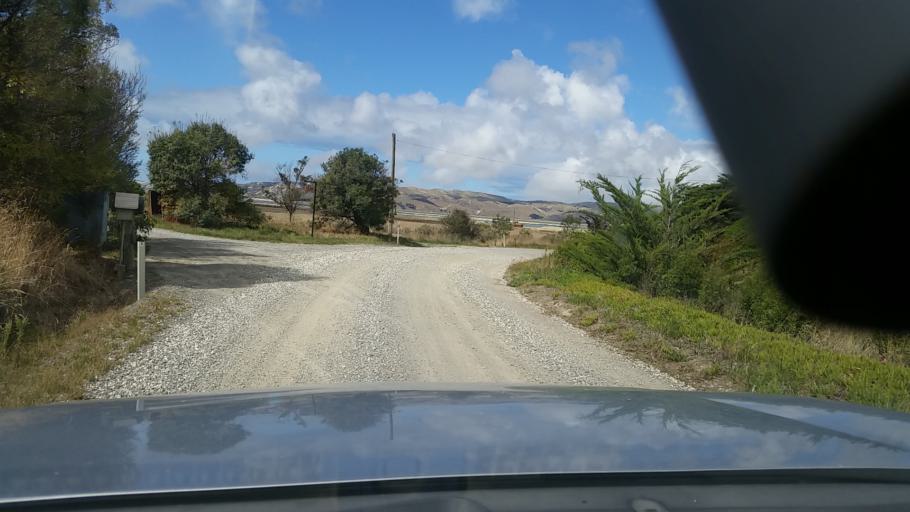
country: NZ
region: Marlborough
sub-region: Marlborough District
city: Blenheim
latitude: -41.7021
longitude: 174.1495
